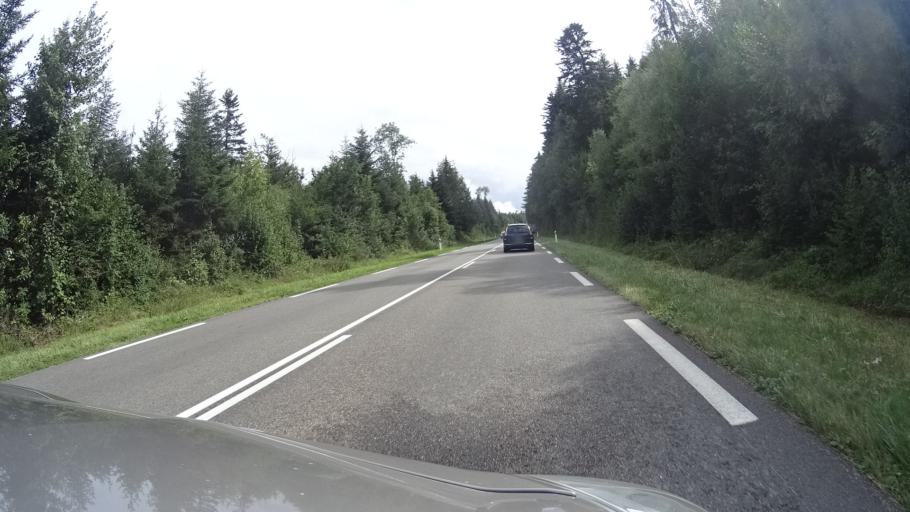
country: FR
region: Franche-Comte
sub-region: Departement du Jura
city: Champagnole
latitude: 46.7076
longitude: 5.9311
